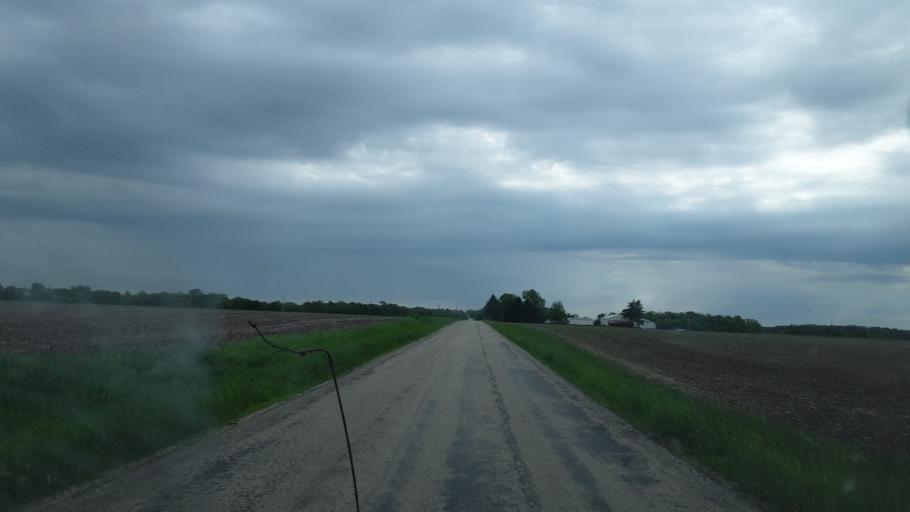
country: US
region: Illinois
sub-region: Fulton County
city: Astoria
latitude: 40.3644
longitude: -90.4635
